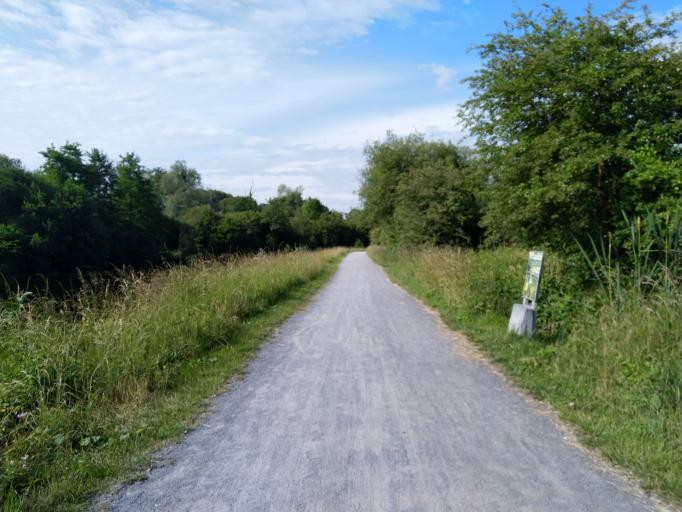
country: FR
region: Nord-Pas-de-Calais
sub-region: Departement du Nord
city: Marpent
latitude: 50.2875
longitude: 4.0676
